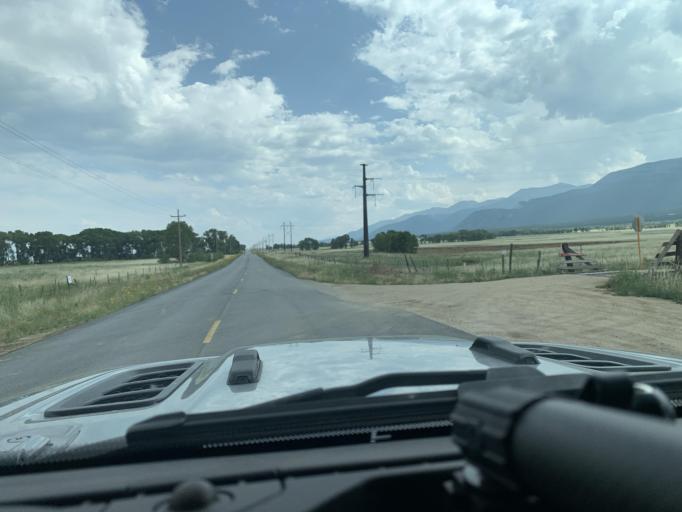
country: US
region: Colorado
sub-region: Chaffee County
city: Buena Vista
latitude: 38.7963
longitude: -106.1465
